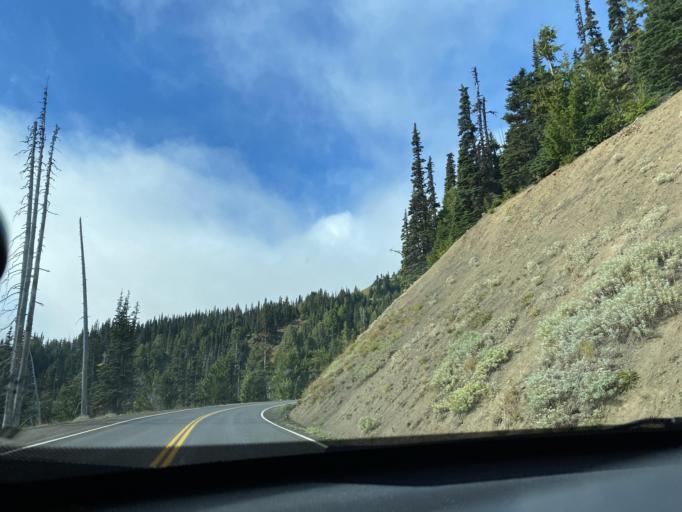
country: US
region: Washington
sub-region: Clallam County
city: Port Angeles
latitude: 47.9782
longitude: -123.4728
